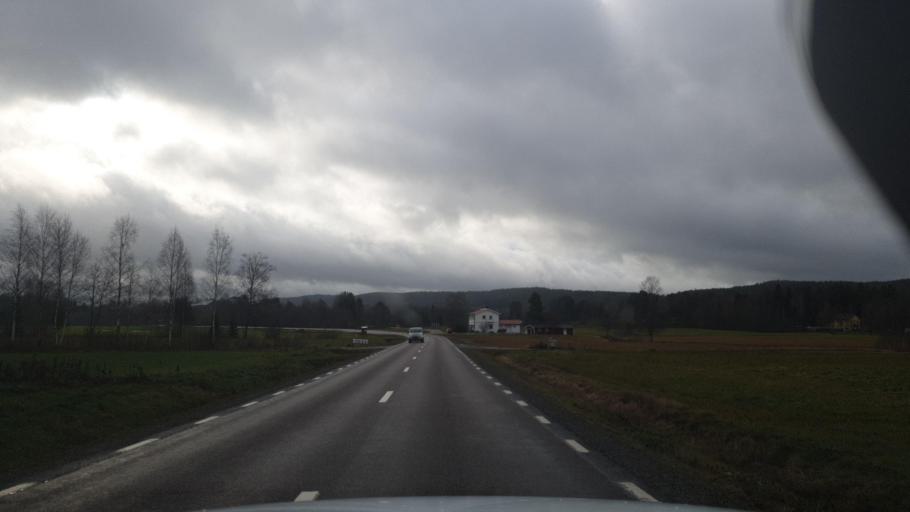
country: SE
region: Vaermland
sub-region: Arjangs Kommun
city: Arjaeng
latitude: 59.6385
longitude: 12.1363
